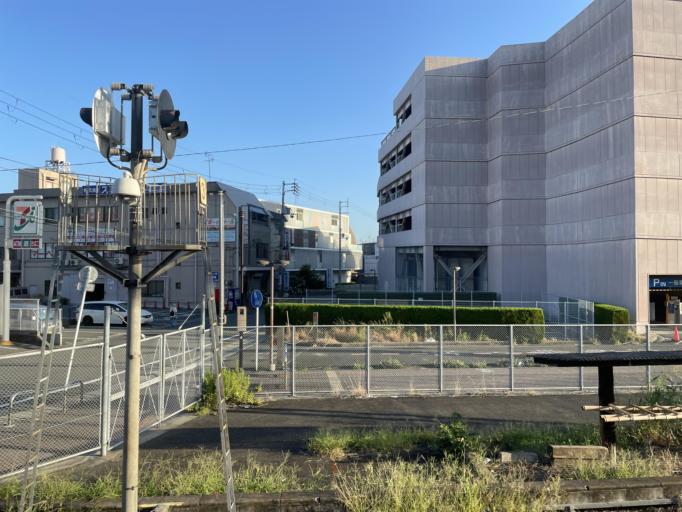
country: JP
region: Osaka
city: Kashihara
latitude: 34.5717
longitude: 135.5927
